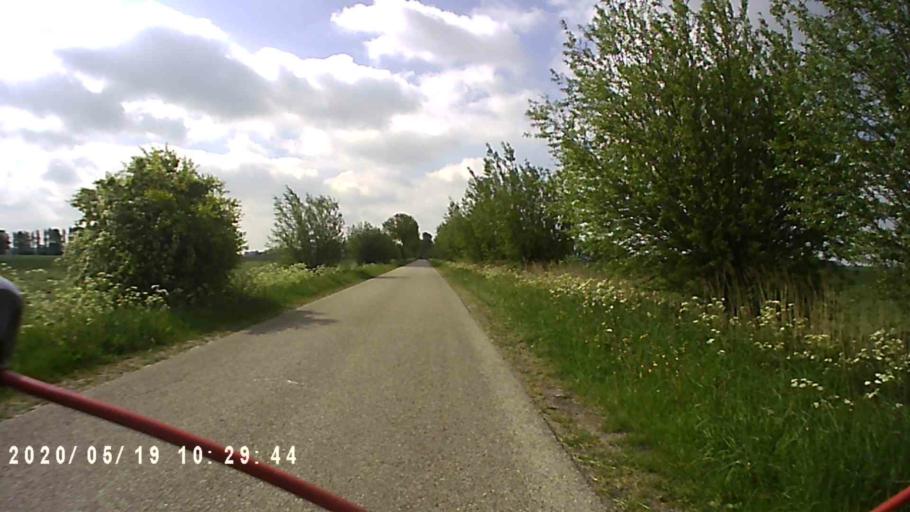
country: NL
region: Friesland
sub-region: Gemeente Kollumerland en Nieuwkruisland
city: Kollum
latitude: 53.2972
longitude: 6.1956
